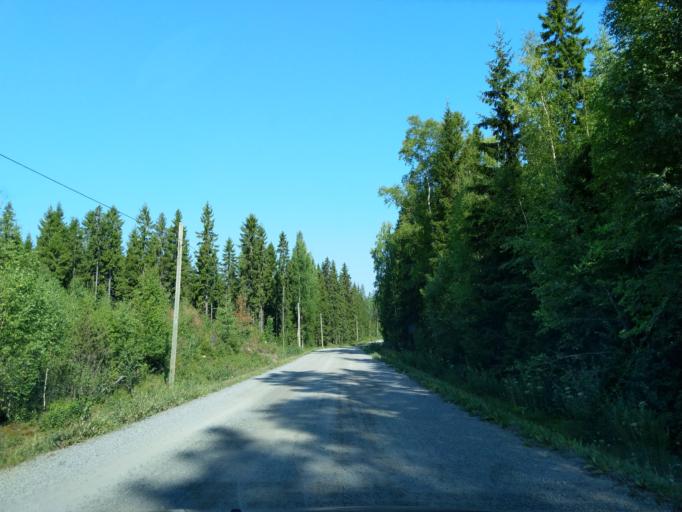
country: FI
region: Satakunta
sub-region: Pori
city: Laengelmaeki
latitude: 61.7263
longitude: 22.1879
